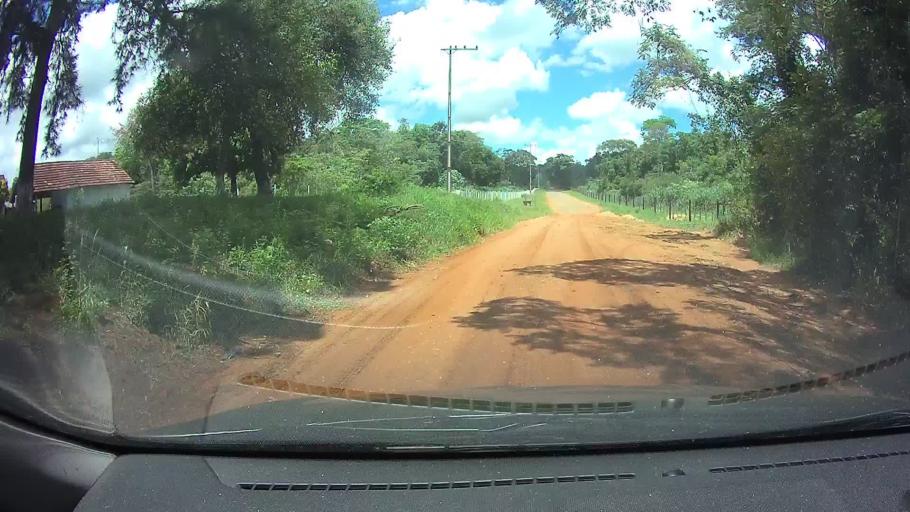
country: PY
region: Paraguari
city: La Colmena
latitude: -25.9170
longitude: -56.7948
